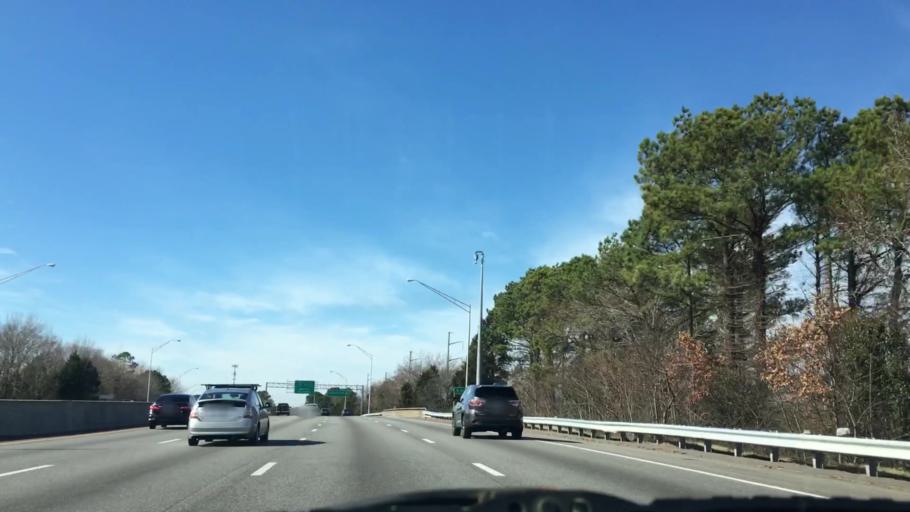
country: US
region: Virginia
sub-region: City of Virginia Beach
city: Virginia Beach
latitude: 36.8362
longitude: -76.0887
